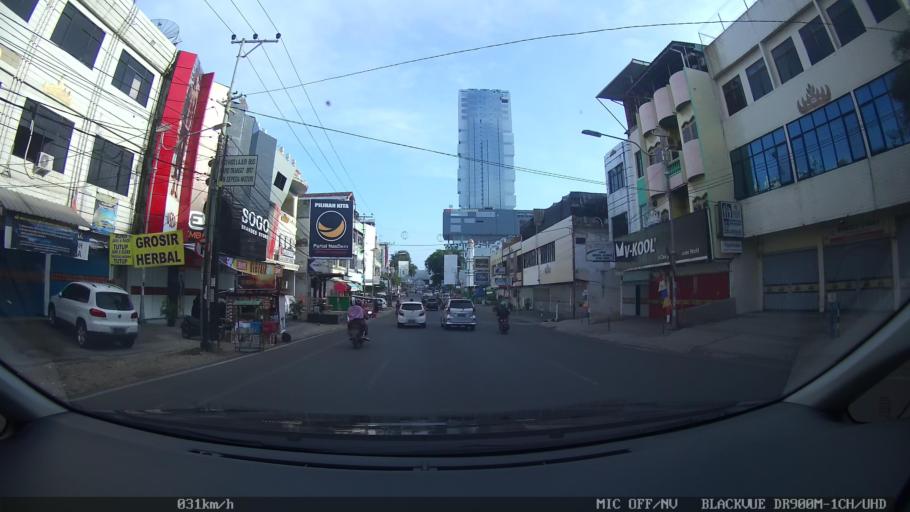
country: ID
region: Lampung
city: Bandarlampung
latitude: -5.4136
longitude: 105.2584
